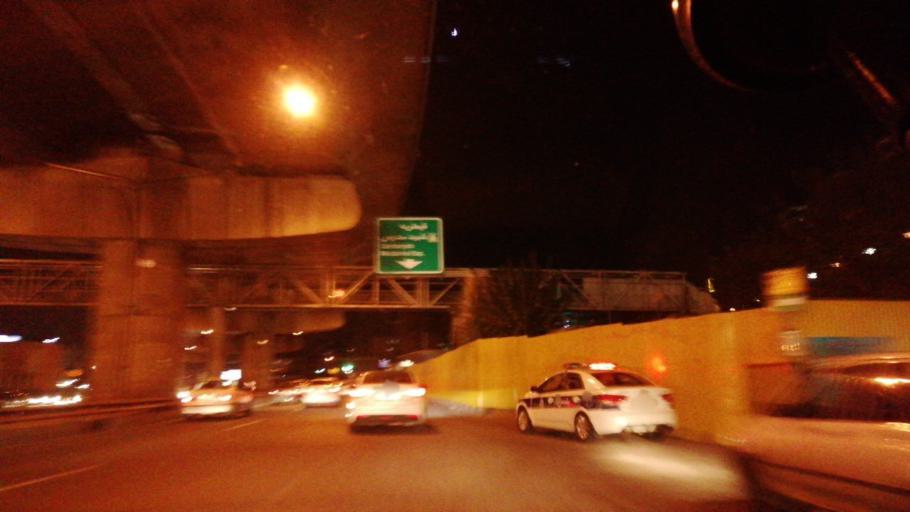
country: IR
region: Tehran
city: Tajrish
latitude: 35.7903
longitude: 51.4802
